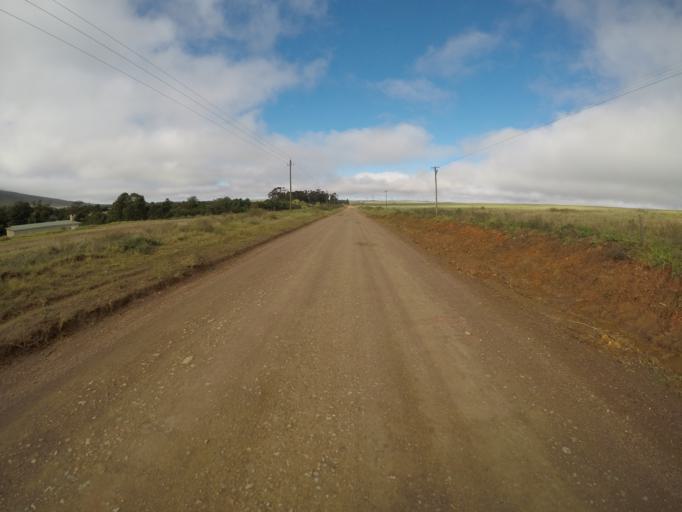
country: ZA
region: Western Cape
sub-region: Cape Winelands District Municipality
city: Ashton
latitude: -34.1351
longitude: 19.8578
